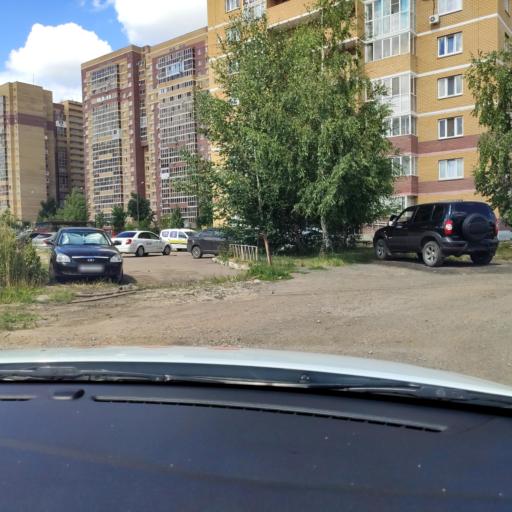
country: RU
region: Tatarstan
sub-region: Gorod Kazan'
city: Kazan
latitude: 55.7794
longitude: 49.2414
